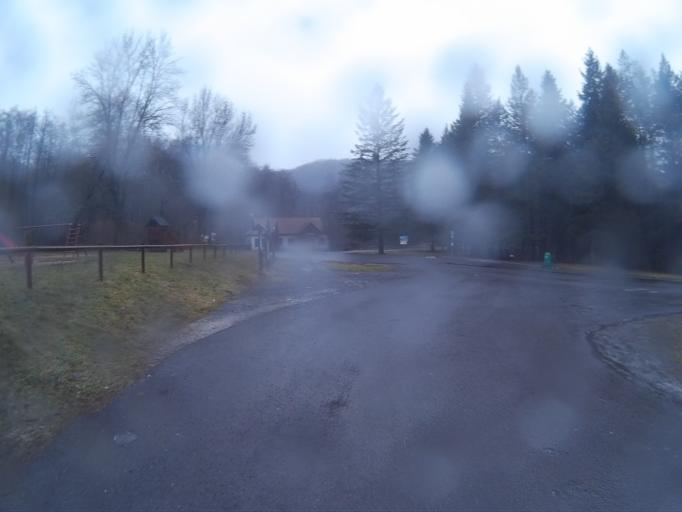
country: HU
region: Nograd
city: Somoskoujfalu
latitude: 48.1558
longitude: 19.8524
